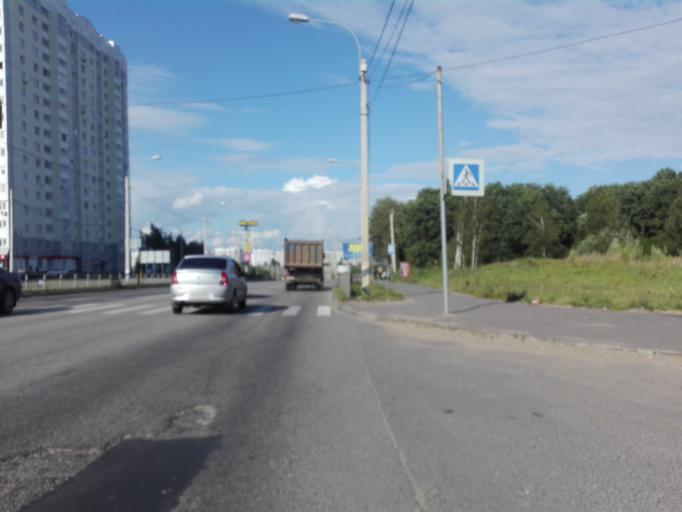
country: RU
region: Orjol
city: Orel
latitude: 53.0039
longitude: 36.1126
